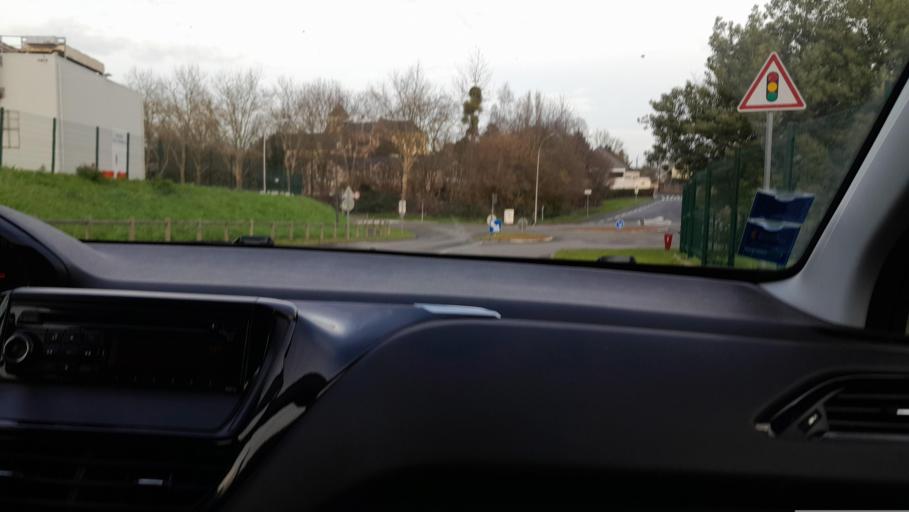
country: FR
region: Pays de la Loire
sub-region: Departement de la Mayenne
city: Craon
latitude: 47.8433
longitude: -0.9594
